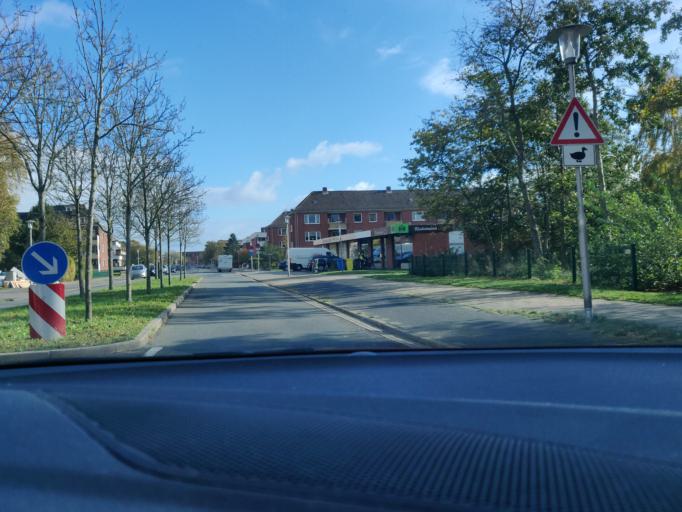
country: DE
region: Lower Saxony
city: Cuxhaven
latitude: 53.8679
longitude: 8.6815
